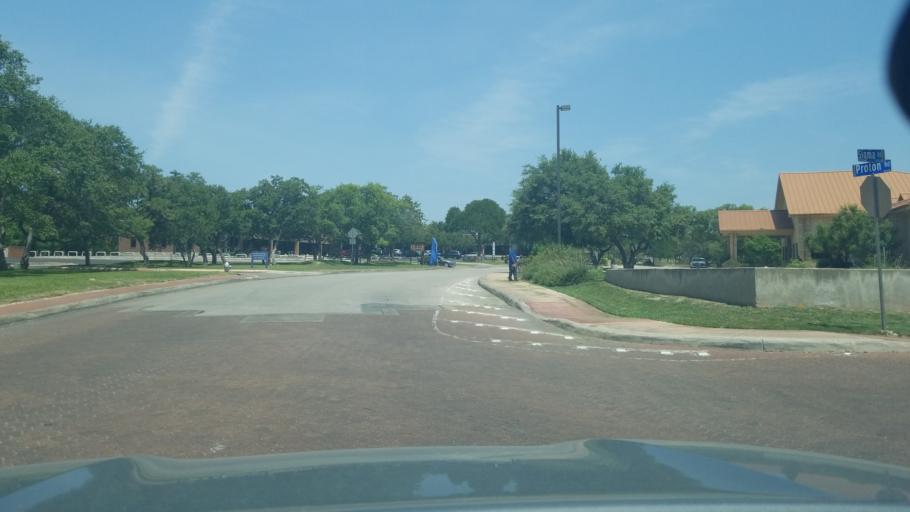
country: US
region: Texas
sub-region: Bexar County
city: Hollywood Park
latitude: 29.6115
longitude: -98.4827
